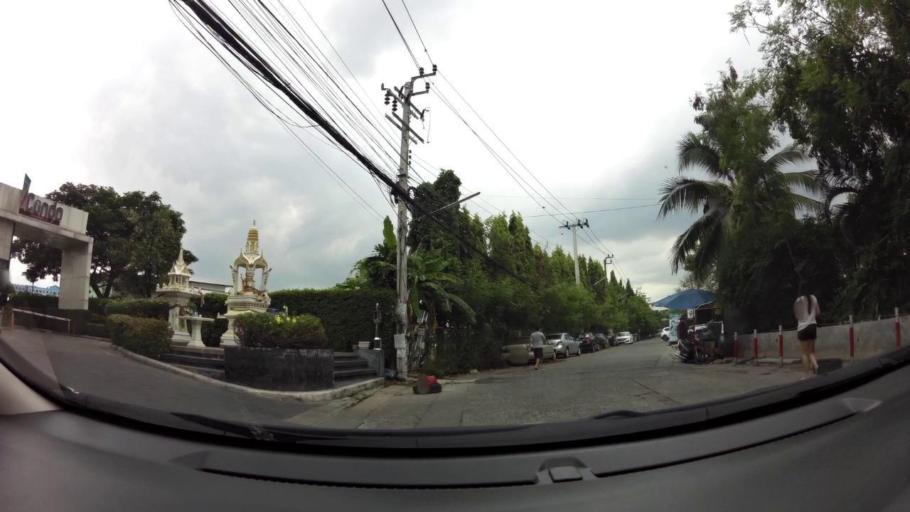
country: TH
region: Bangkok
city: Bang Na
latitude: 13.6765
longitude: 100.6385
